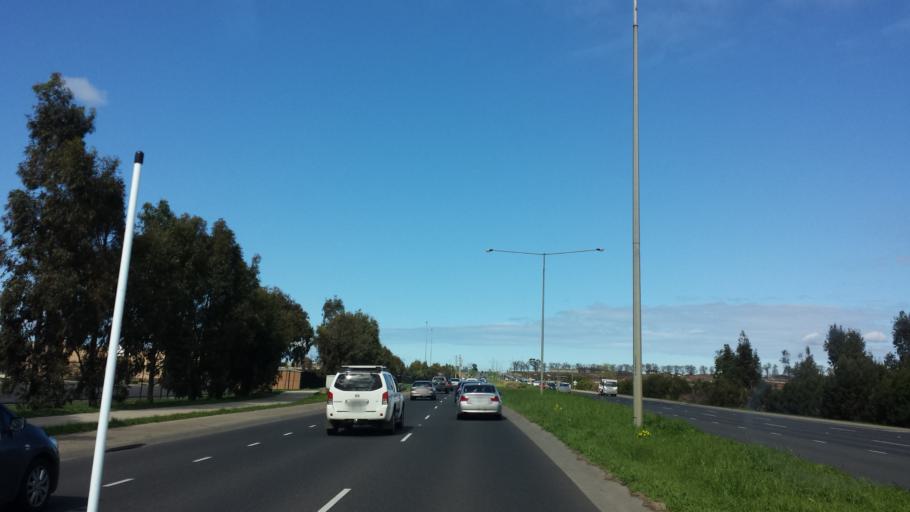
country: AU
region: Victoria
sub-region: Casey
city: Berwick
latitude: -38.0693
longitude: 145.3365
